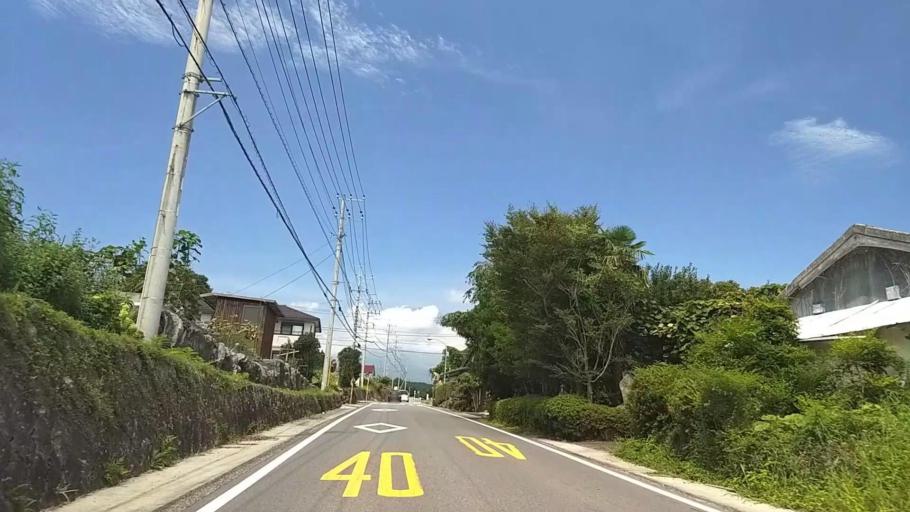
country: JP
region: Shizuoka
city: Gotemba
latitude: 35.2463
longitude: 138.8542
